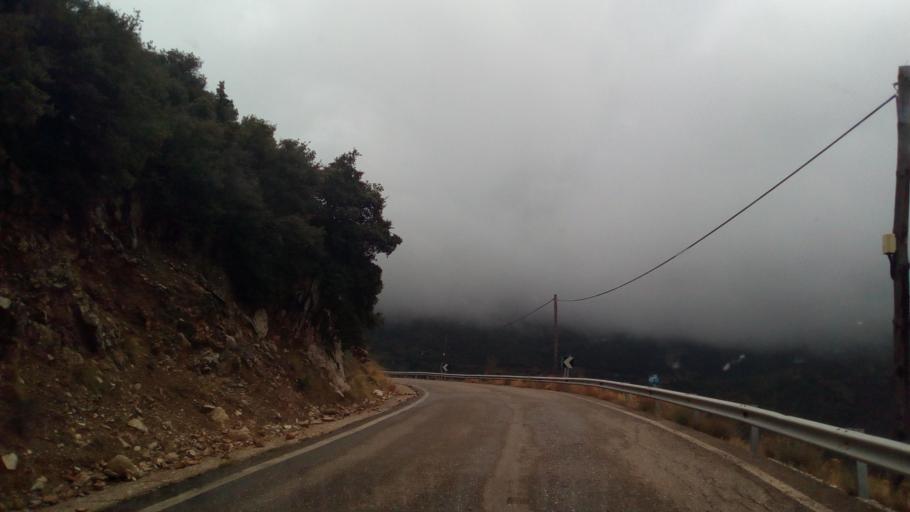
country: GR
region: West Greece
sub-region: Nomos Aitolias kai Akarnanias
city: Nafpaktos
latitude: 38.5225
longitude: 21.8382
